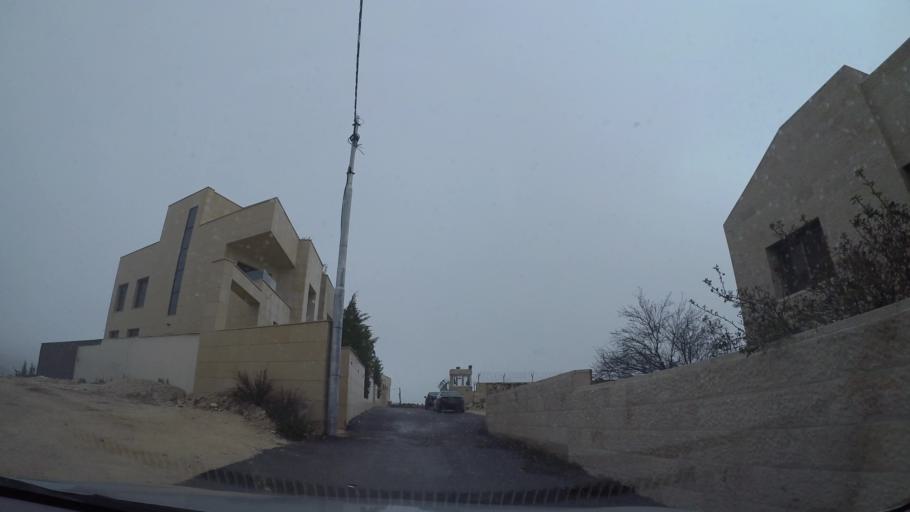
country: JO
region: Amman
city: Wadi as Sir
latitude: 31.9995
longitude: 35.8197
